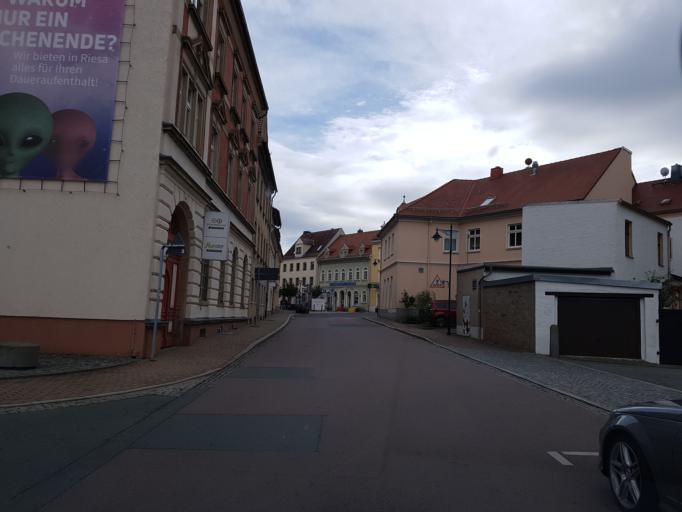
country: DE
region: Saxony
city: Riesa
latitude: 51.3046
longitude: 13.3061
